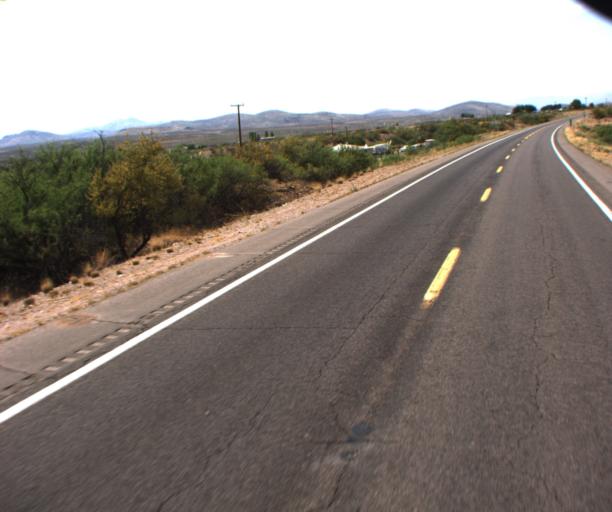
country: US
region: Arizona
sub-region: Greenlee County
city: Clifton
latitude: 32.8157
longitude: -109.1710
